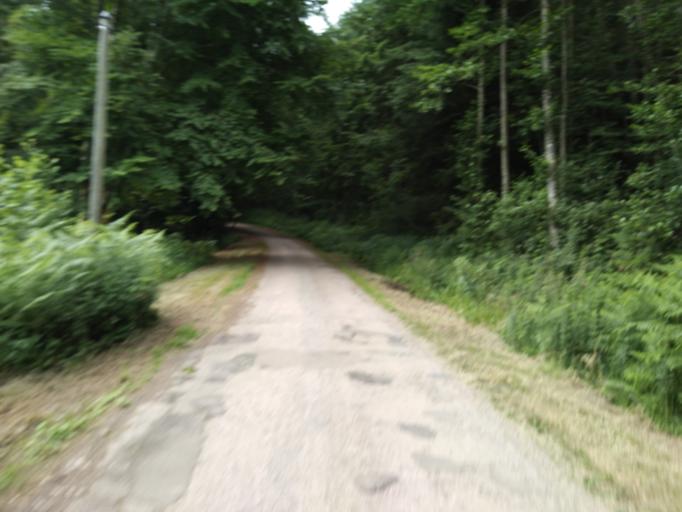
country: FR
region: Bourgogne
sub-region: Departement de la Cote-d'Or
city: Saulieu
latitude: 47.2792
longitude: 4.1215
